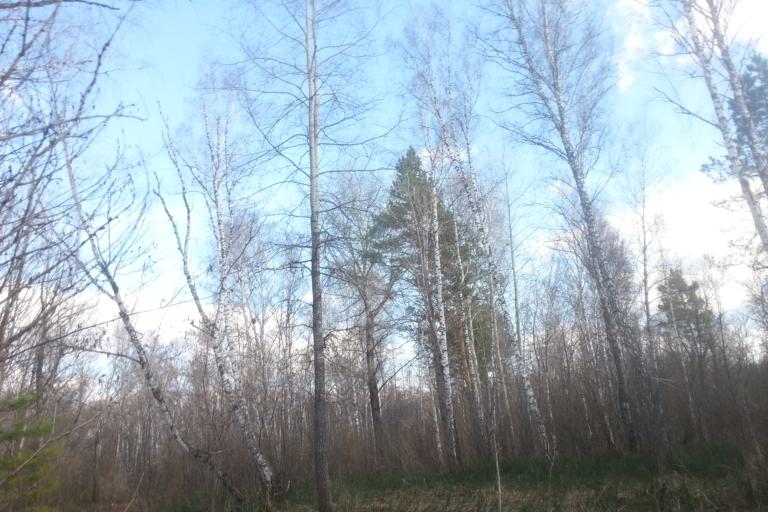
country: RU
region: Altai Krai
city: Sannikovo
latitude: 53.3312
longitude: 84.0214
